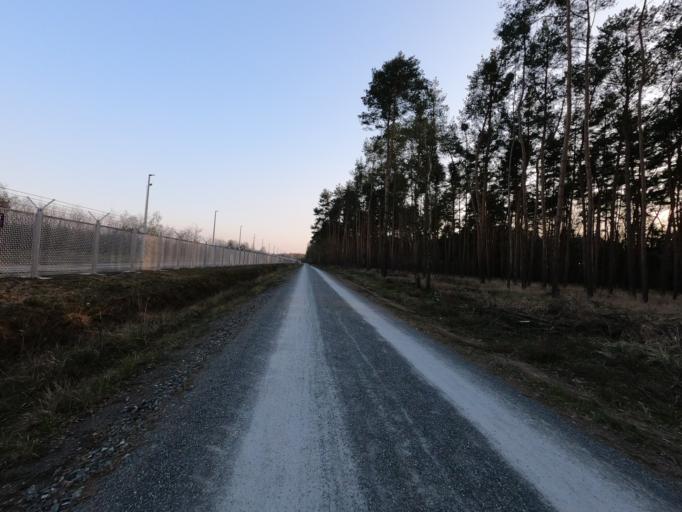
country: DE
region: Hesse
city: Kelsterbach
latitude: 50.0031
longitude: 8.5221
